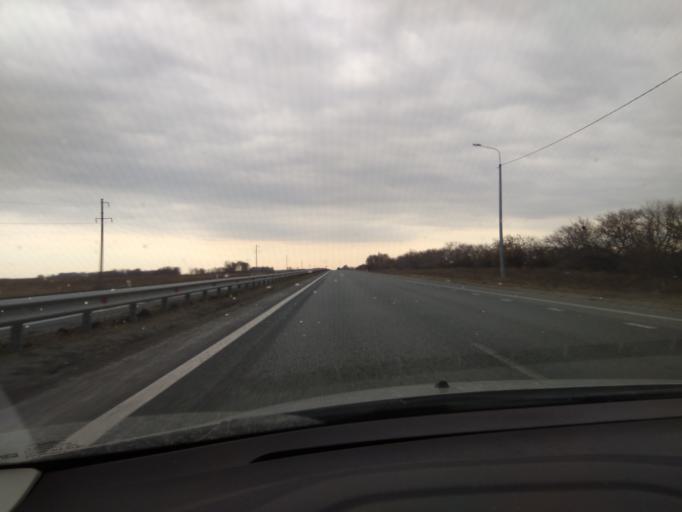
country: RU
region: Chelyabinsk
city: Kunashak
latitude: 55.7444
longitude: 61.2275
